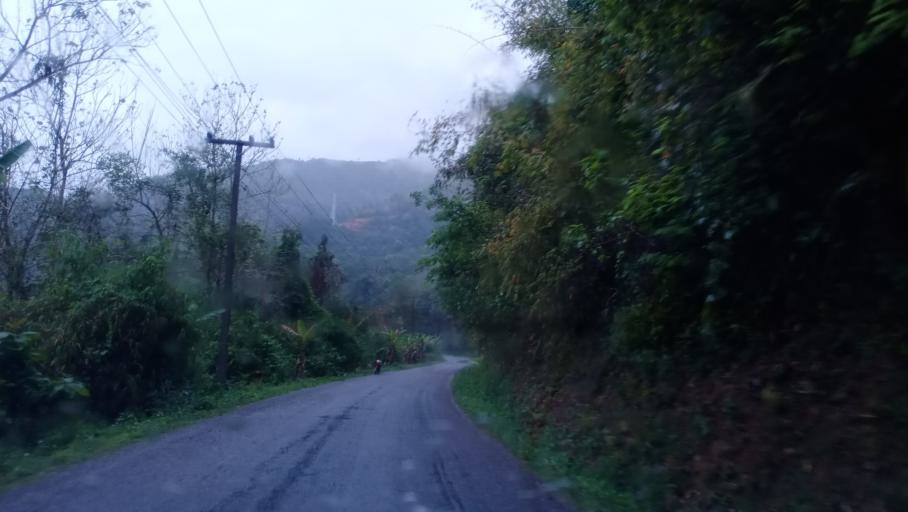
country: LA
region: Phongsali
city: Khoa
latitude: 21.0634
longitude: 102.4803
